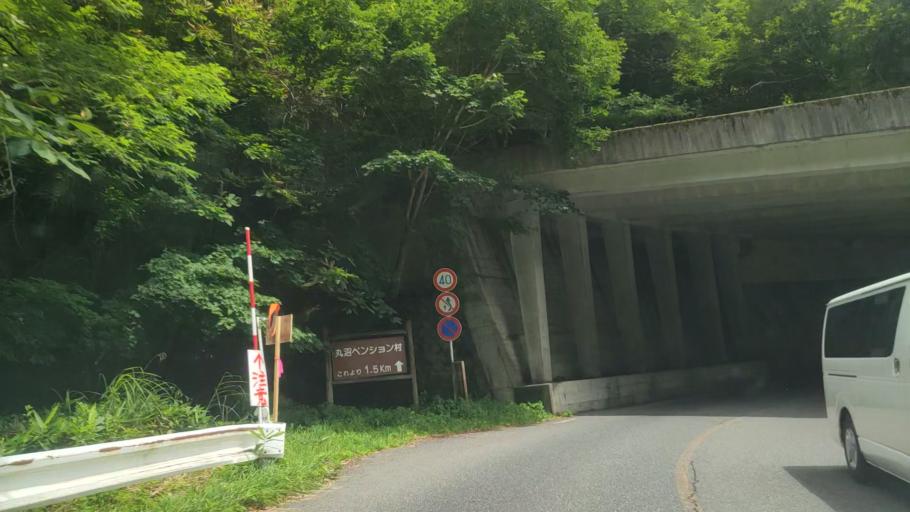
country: JP
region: Tochigi
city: Nikko
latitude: 36.8131
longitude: 139.3120
